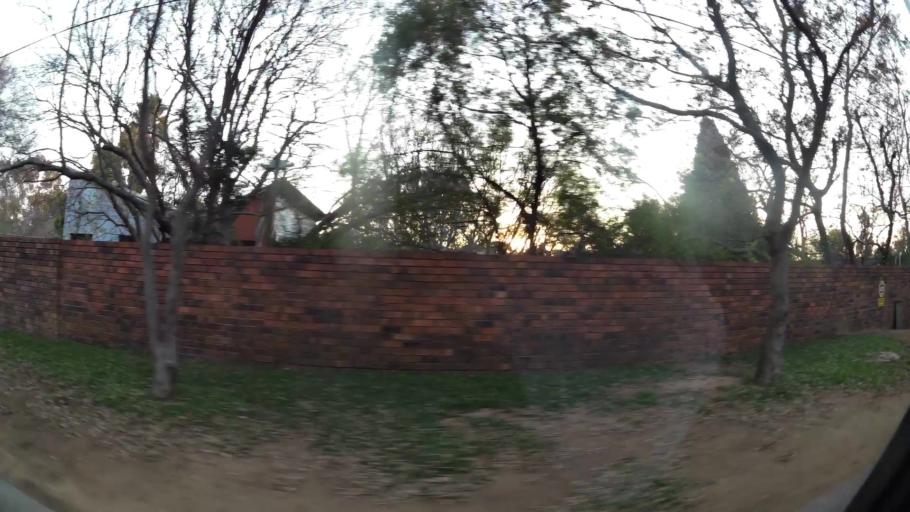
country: ZA
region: Gauteng
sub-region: City of Johannesburg Metropolitan Municipality
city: Diepsloot
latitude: -26.0398
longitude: 27.9863
